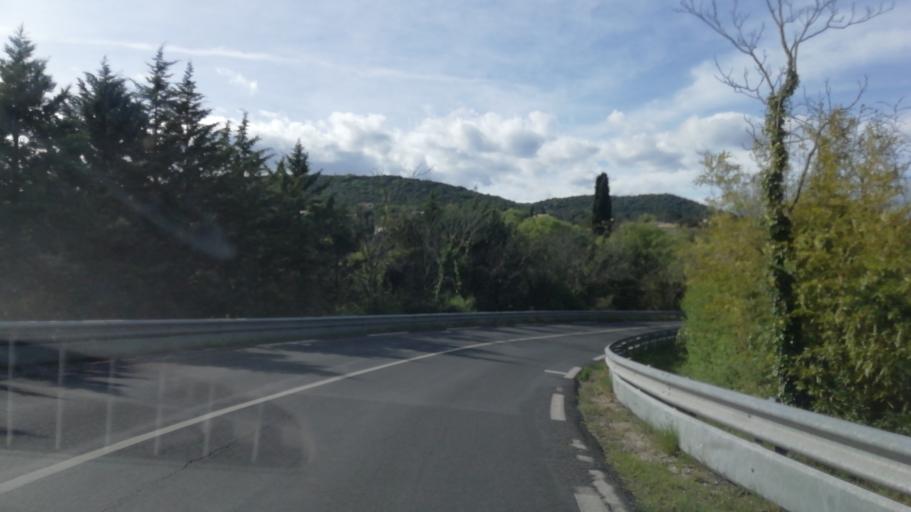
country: FR
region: Languedoc-Roussillon
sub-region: Departement de l'Herault
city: Saint-Martin-de-Londres
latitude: 43.7728
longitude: 3.7209
